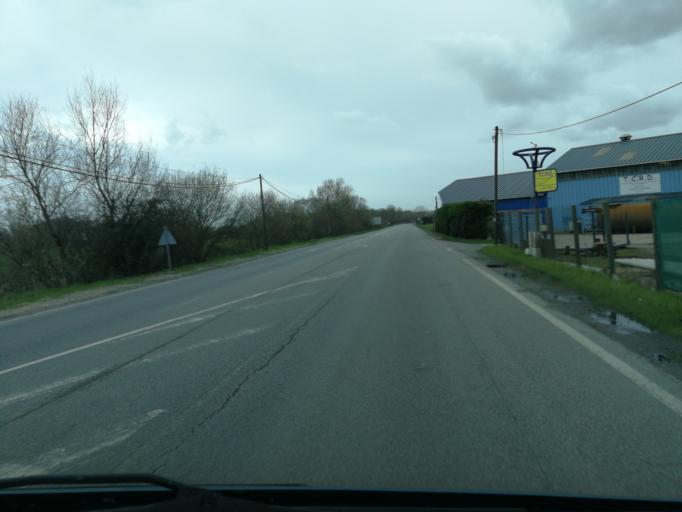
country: FR
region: Haute-Normandie
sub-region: Departement de l'Eure
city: Quillebeuf-sur-Seine
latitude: 49.4844
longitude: 0.5304
